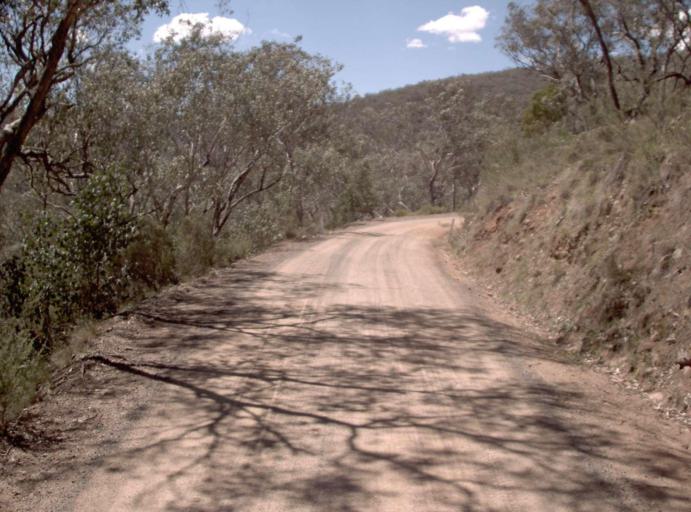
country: AU
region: New South Wales
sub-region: Snowy River
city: Jindabyne
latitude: -37.0502
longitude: 148.5384
